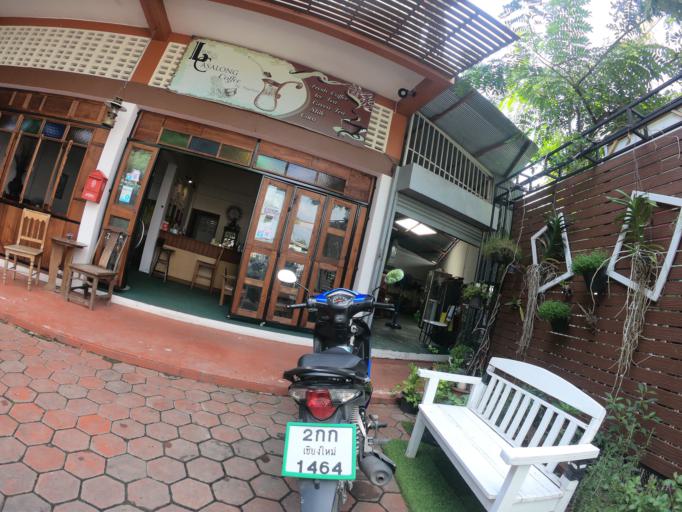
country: TH
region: Chiang Mai
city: Chiang Mai
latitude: 18.7762
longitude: 98.9914
